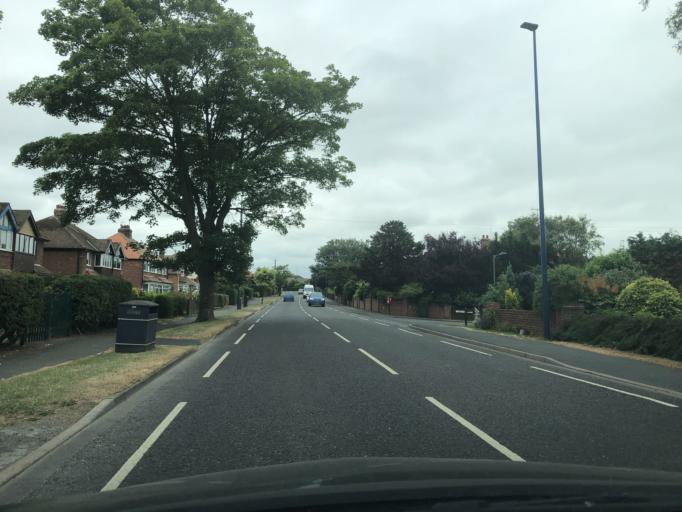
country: GB
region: England
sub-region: North Yorkshire
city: Filey
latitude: 54.2076
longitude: -0.2990
